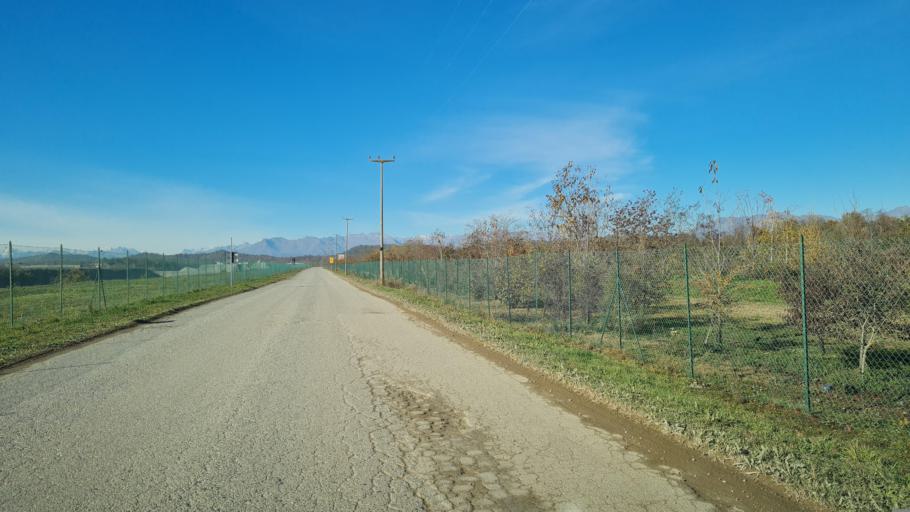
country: IT
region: Piedmont
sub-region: Provincia di Biella
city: Cavaglia
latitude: 45.3825
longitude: 8.1075
